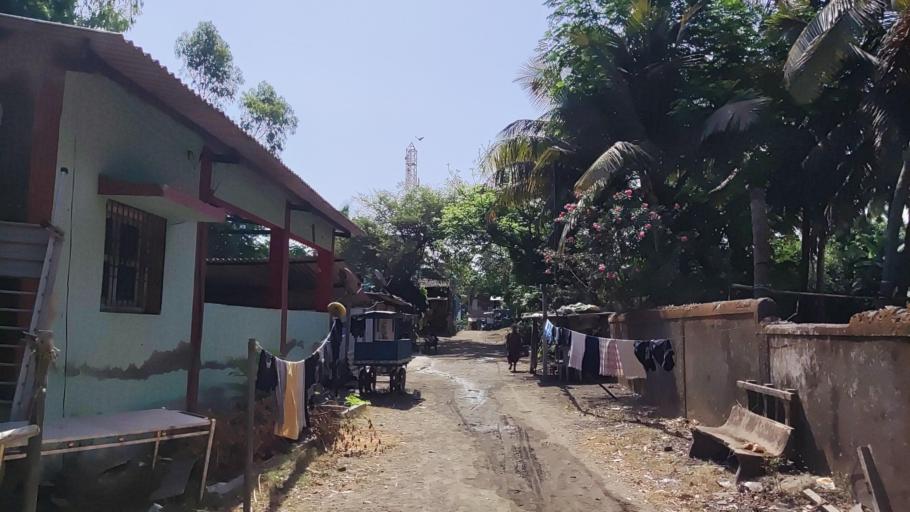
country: IN
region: Daman and Diu
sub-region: Daman District
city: Daman
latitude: 20.3912
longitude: 72.8290
